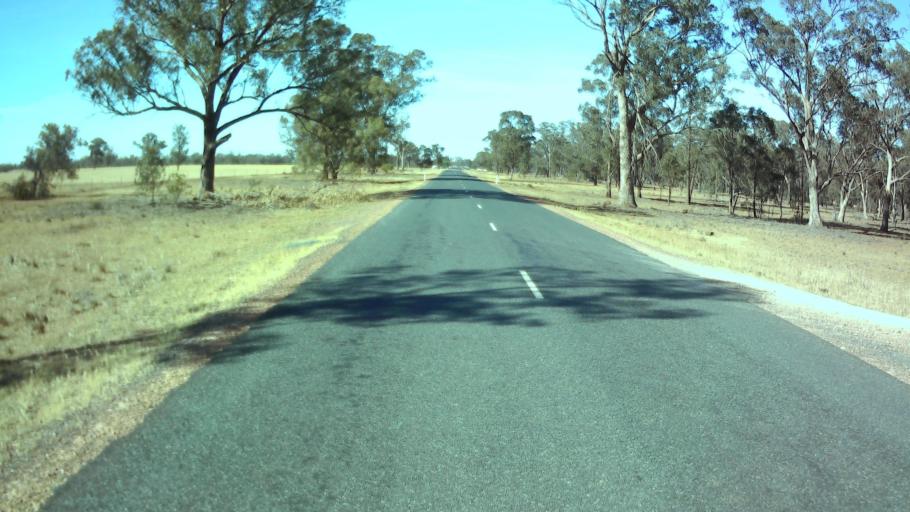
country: AU
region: New South Wales
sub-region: Weddin
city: Grenfell
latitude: -34.0923
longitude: 147.8881
